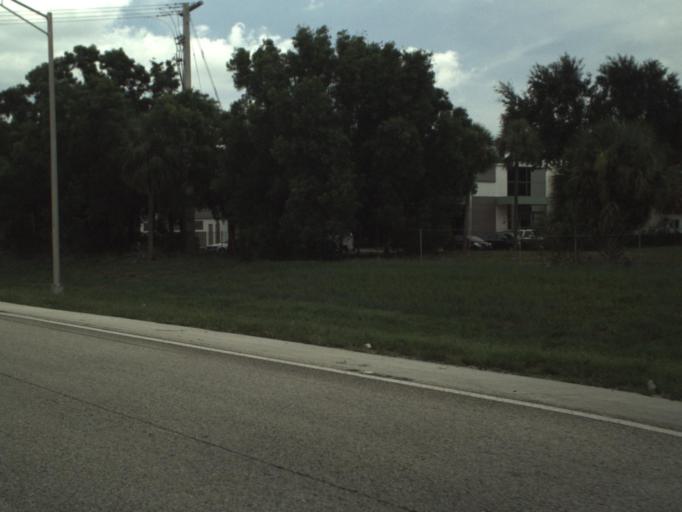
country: US
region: Florida
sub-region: Broward County
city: Deerfield Beach
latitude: 26.3251
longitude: -80.1165
